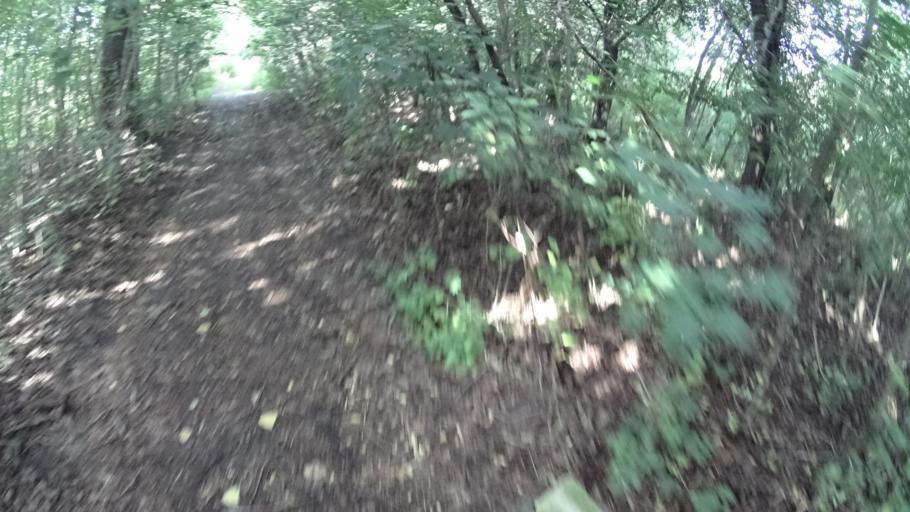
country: PL
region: Masovian Voivodeship
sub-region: Powiat piaseczynski
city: Lesznowola
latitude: 52.0249
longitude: 20.9045
